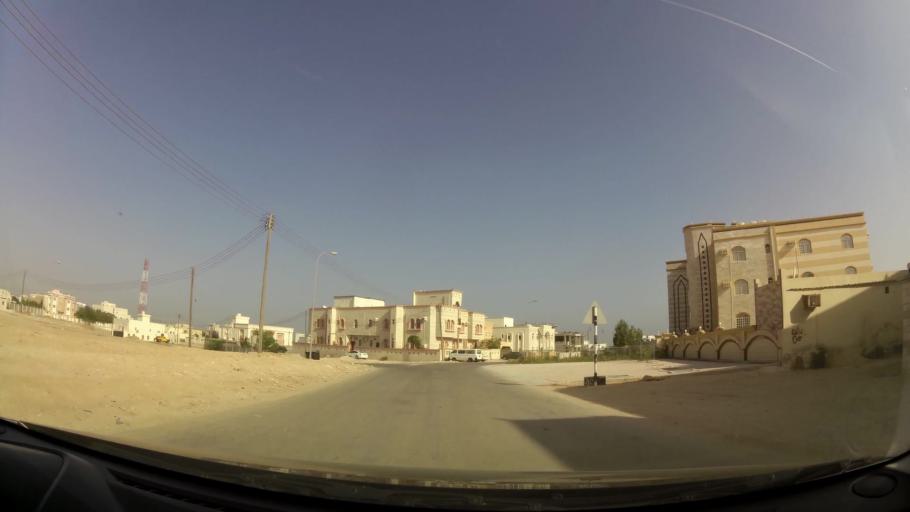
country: OM
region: Zufar
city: Salalah
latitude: 17.0015
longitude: 54.0224
